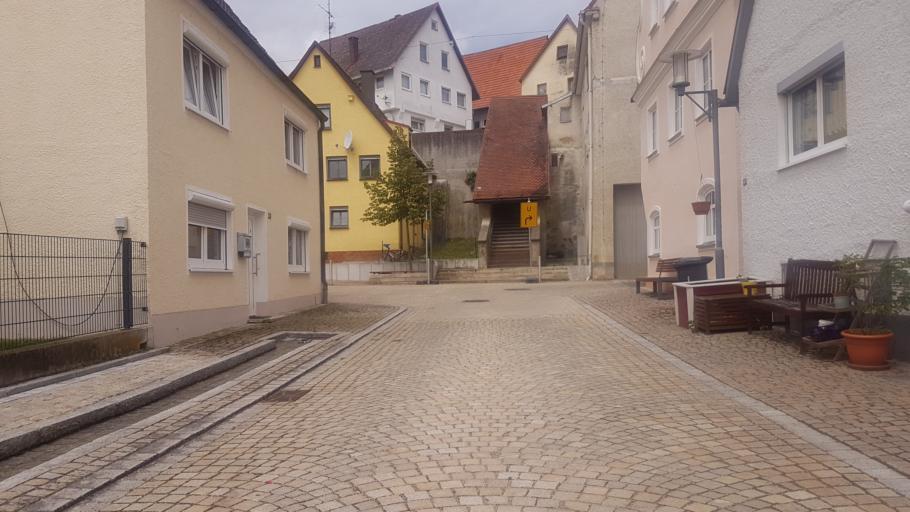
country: DE
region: Bavaria
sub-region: Swabia
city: Lauingen
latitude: 48.5675
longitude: 10.4313
